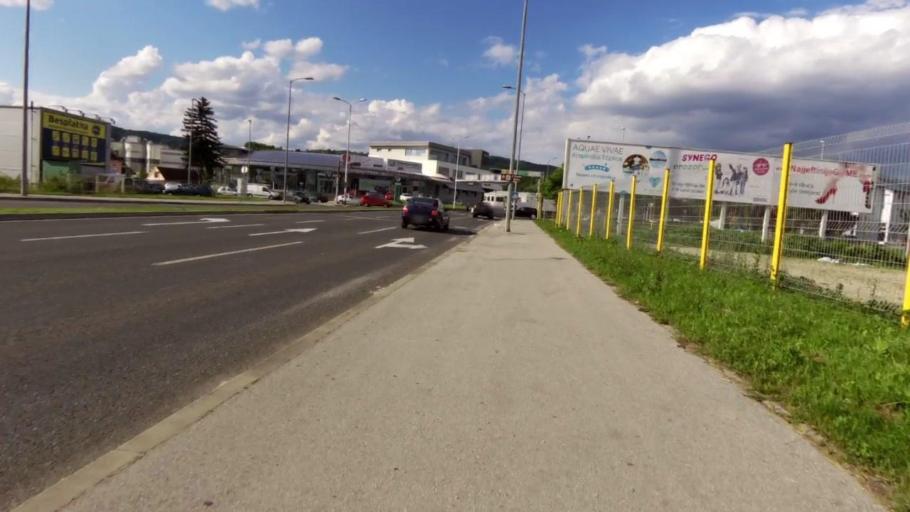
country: HR
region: Grad Zagreb
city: Stenjevec
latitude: 45.8118
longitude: 15.8604
